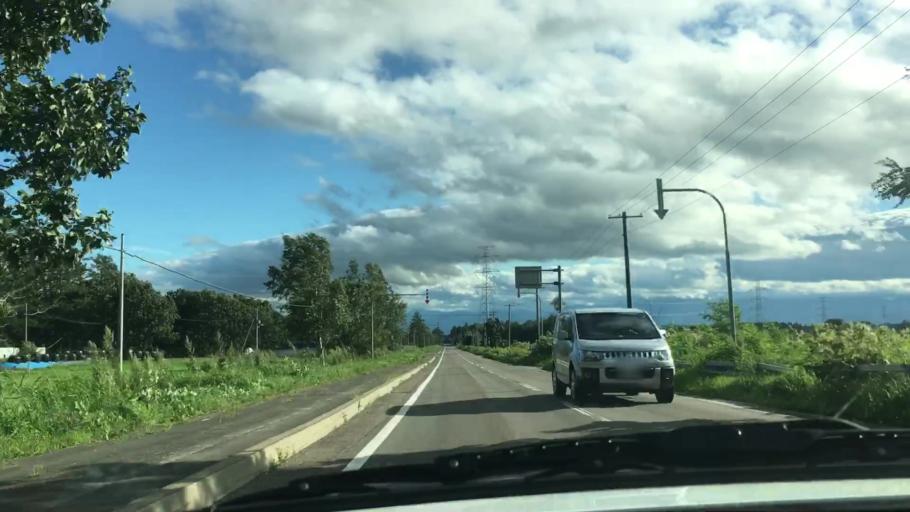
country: JP
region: Hokkaido
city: Otofuke
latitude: 43.1787
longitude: 143.0080
